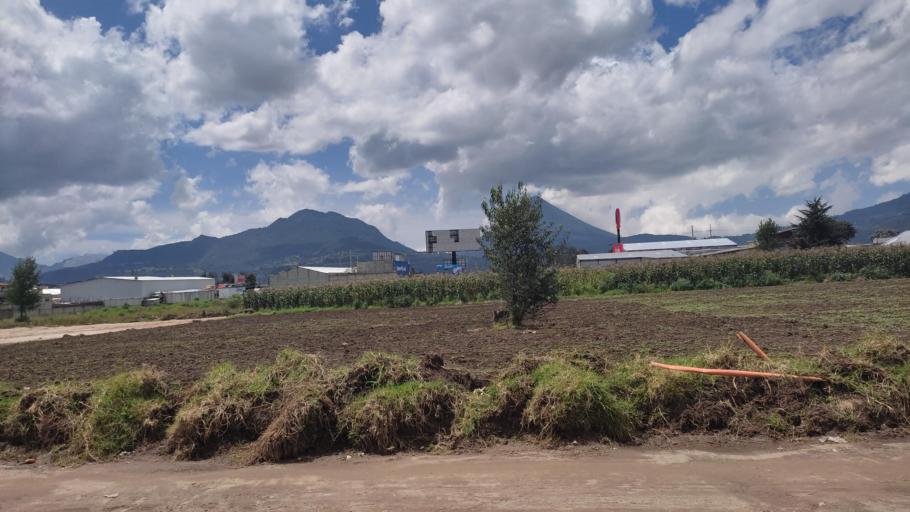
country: GT
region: Quetzaltenango
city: Olintepeque
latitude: 14.8631
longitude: -91.5251
